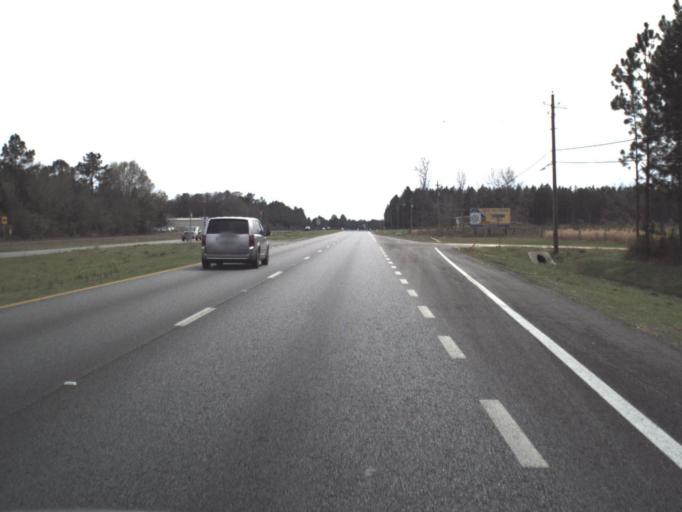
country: US
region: Florida
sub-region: Bay County
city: Youngstown
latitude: 30.3496
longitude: -85.4403
